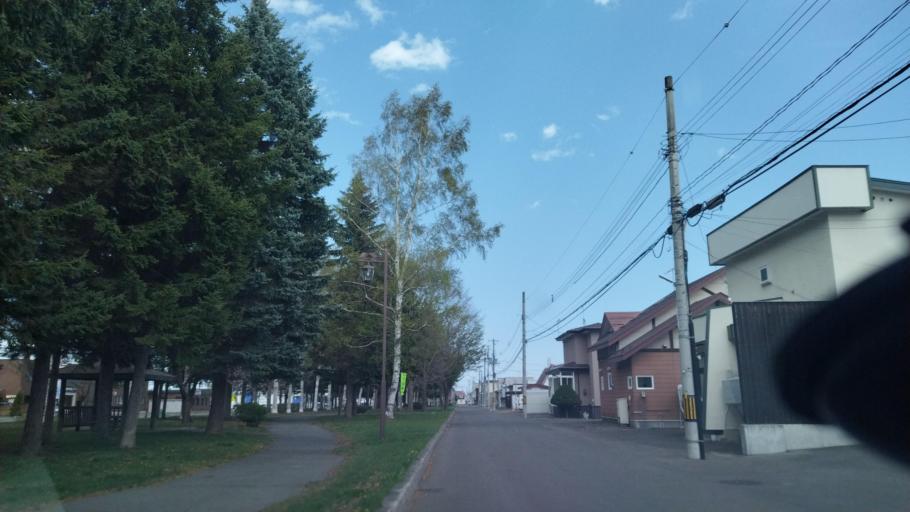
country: JP
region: Hokkaido
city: Obihiro
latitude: 42.9082
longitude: 143.1567
